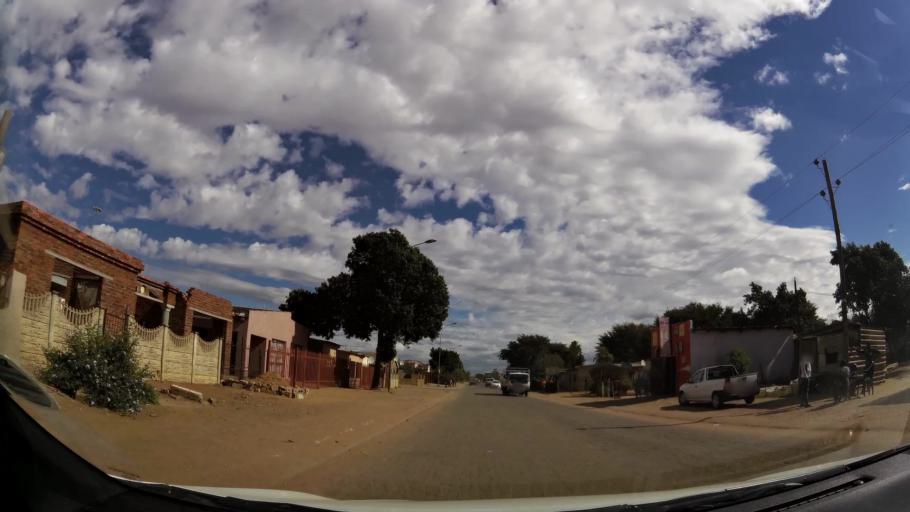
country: ZA
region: Limpopo
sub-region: Waterberg District Municipality
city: Bela-Bela
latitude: -24.8859
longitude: 28.3192
